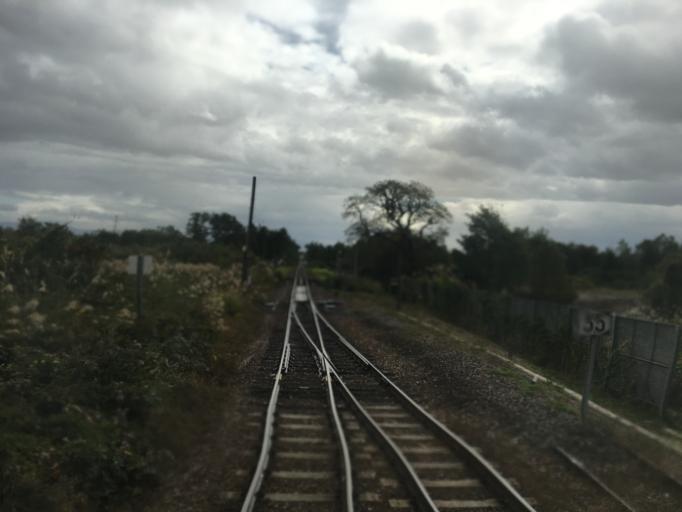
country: JP
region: Yamagata
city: Nagai
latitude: 38.0686
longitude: 140.0313
